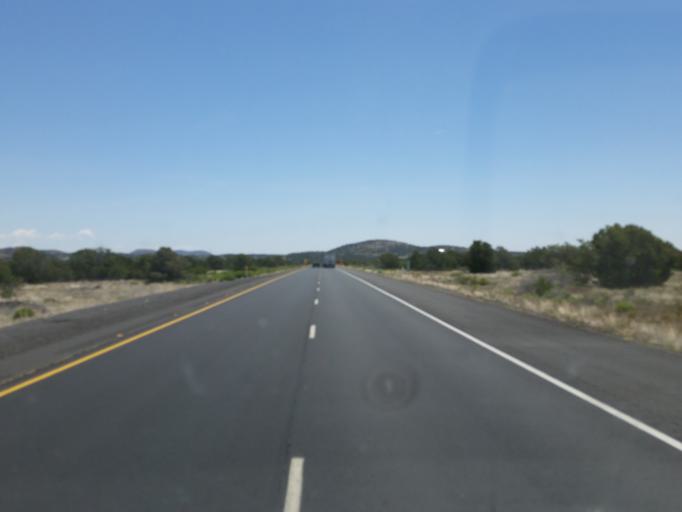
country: US
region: Arizona
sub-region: Coconino County
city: Flagstaff
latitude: 35.2017
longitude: -111.4464
